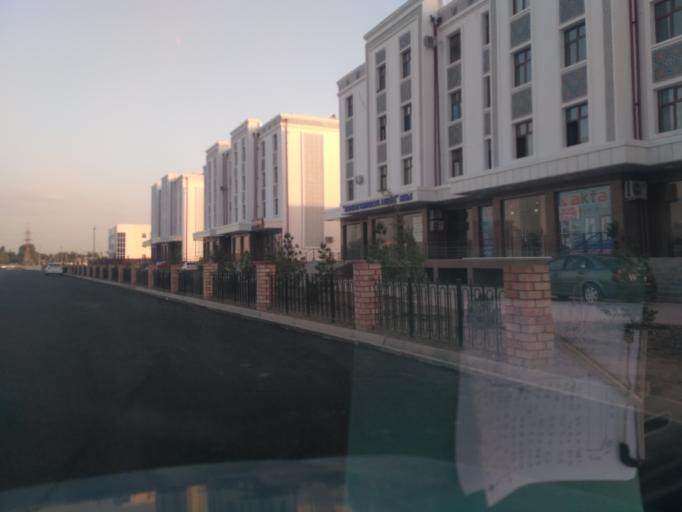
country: UZ
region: Sirdaryo
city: Guliston
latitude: 40.5071
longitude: 68.7673
